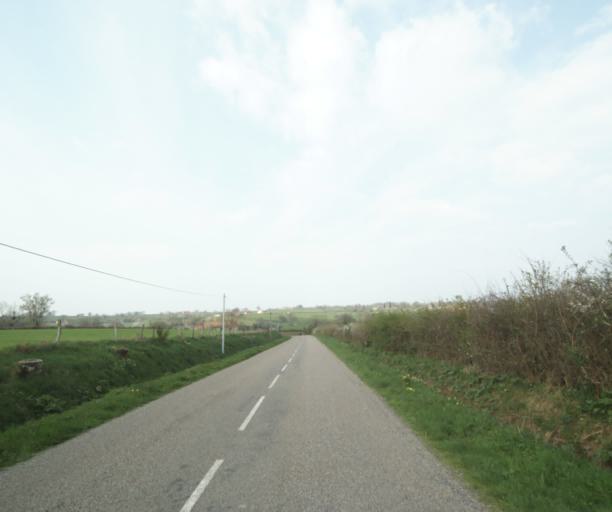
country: FR
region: Bourgogne
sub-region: Departement de Saone-et-Loire
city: Charolles
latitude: 46.4485
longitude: 4.4285
